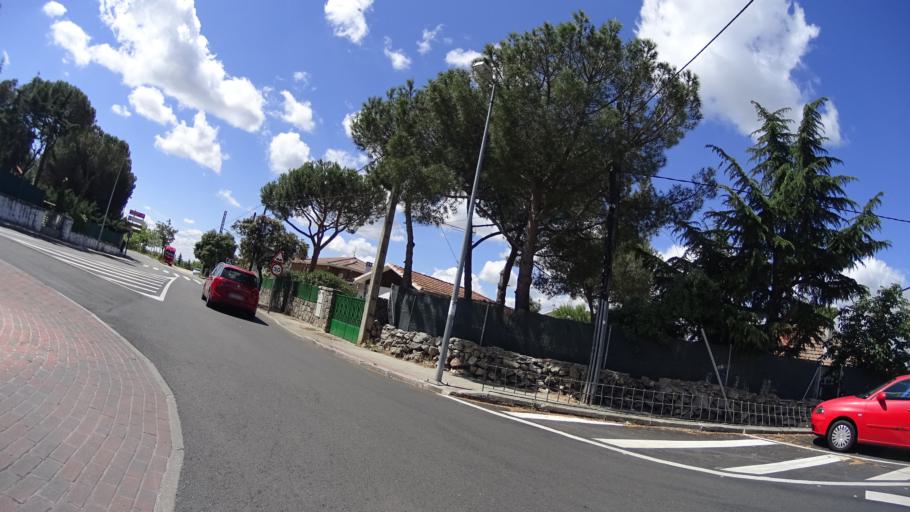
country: ES
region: Madrid
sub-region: Provincia de Madrid
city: Colmenarejo
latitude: 40.5599
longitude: -4.0124
